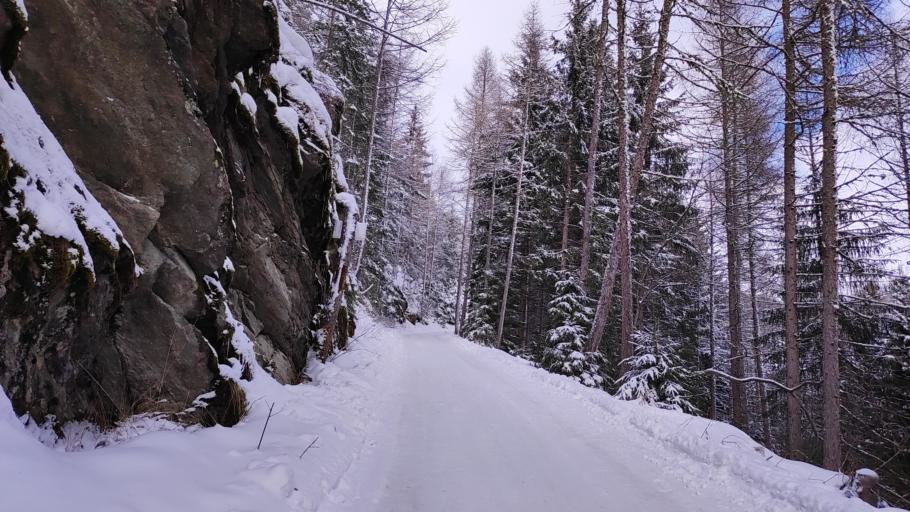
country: AT
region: Tyrol
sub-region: Politischer Bezirk Imst
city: Umhausen
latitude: 47.0986
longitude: 10.9368
